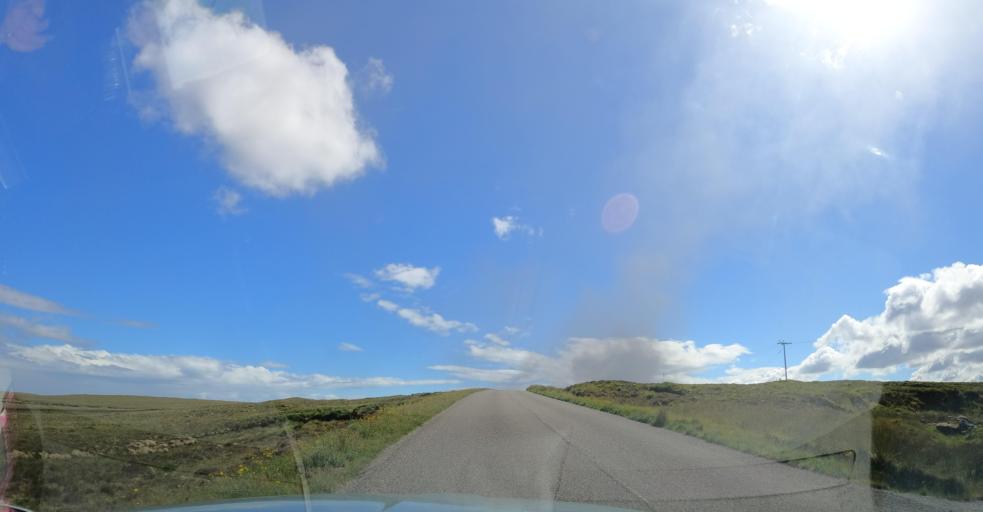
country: GB
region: Scotland
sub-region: Eilean Siar
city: Isle of Lewis
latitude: 58.2850
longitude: -6.4394
